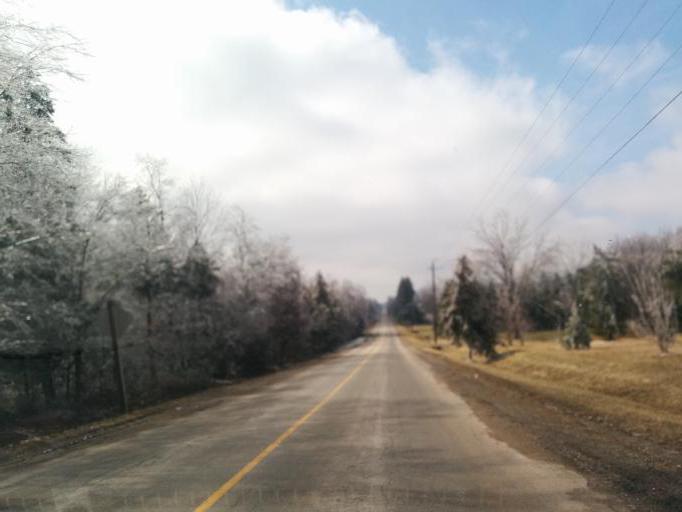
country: CA
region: Ontario
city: Waterloo
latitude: 43.6333
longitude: -80.5539
